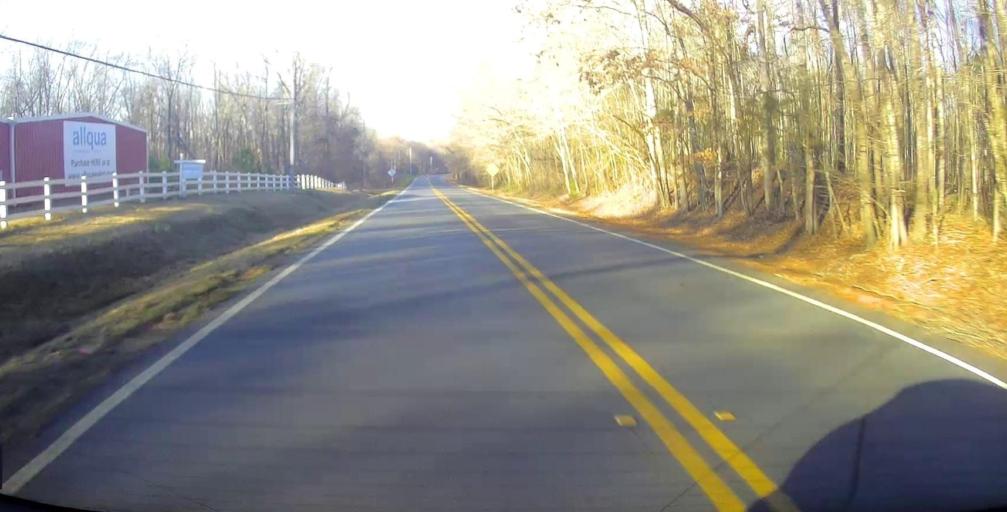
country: US
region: Georgia
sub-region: Harris County
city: Pine Mountain
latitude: 32.9108
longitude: -84.8019
